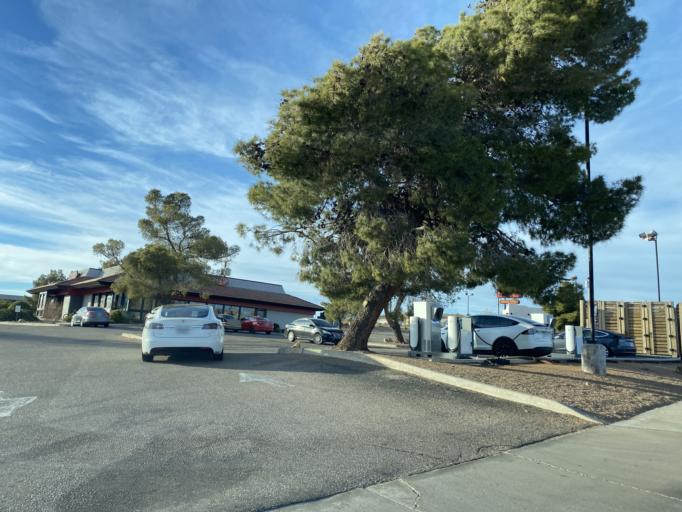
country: US
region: Arizona
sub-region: Mohave County
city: Kingman
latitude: 35.1911
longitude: -114.0654
